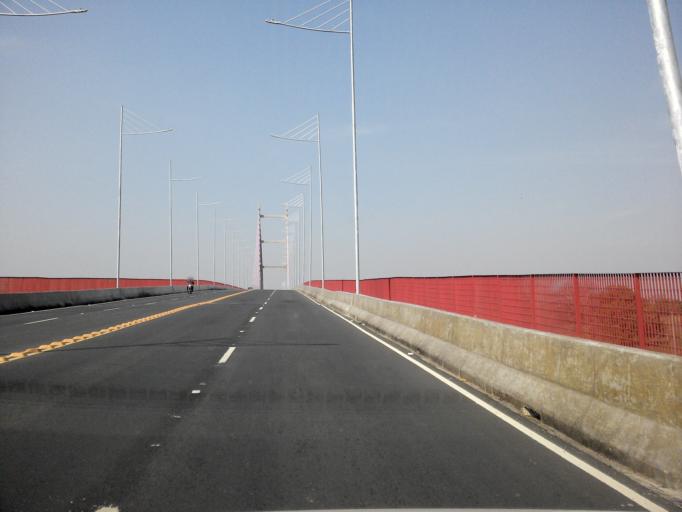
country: BR
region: Sao Paulo
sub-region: Hortolandia
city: Hortolandia
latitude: -22.8776
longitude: -47.1919
